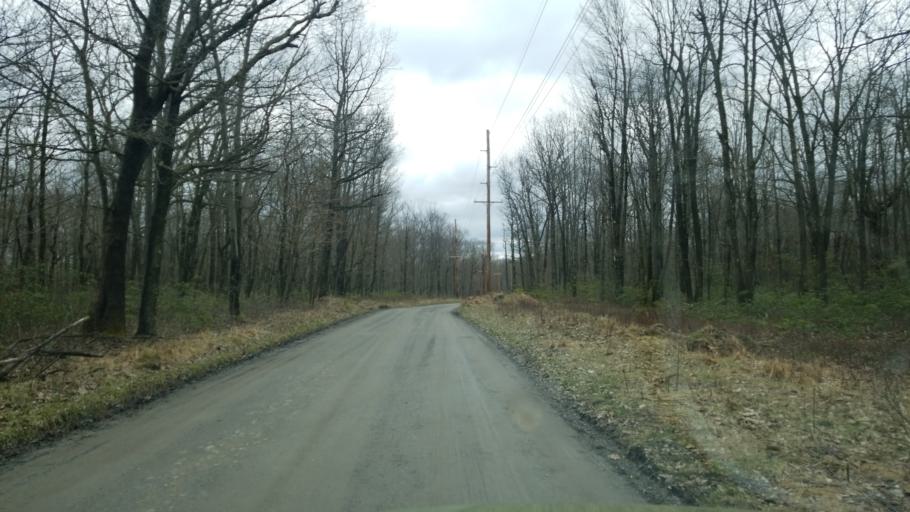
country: US
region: Pennsylvania
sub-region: Clearfield County
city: Shiloh
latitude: 41.1728
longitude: -78.2984
